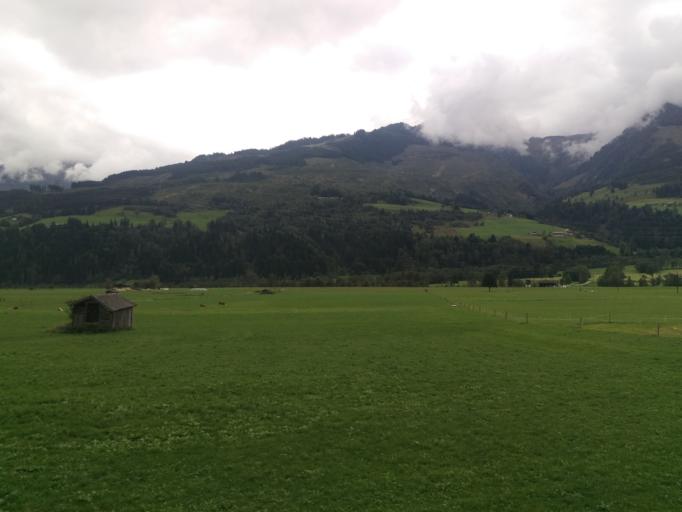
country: AT
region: Salzburg
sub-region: Politischer Bezirk Zell am See
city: Piesendorf
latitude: 47.2865
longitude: 12.7005
